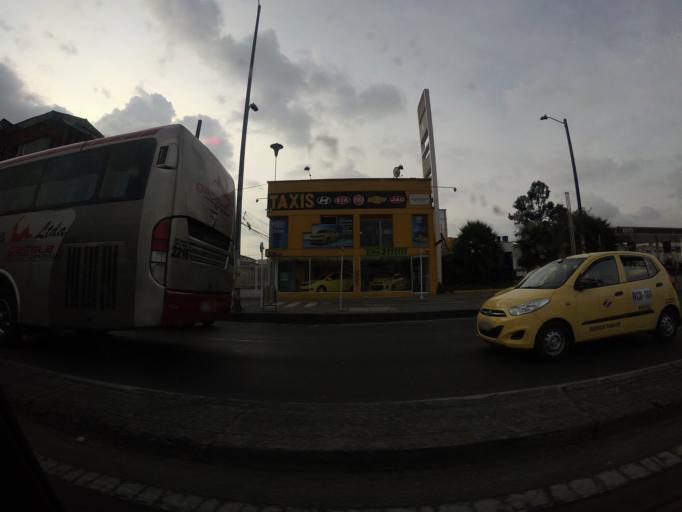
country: CO
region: Bogota D.C.
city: Bogota
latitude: 4.6727
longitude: -74.1057
